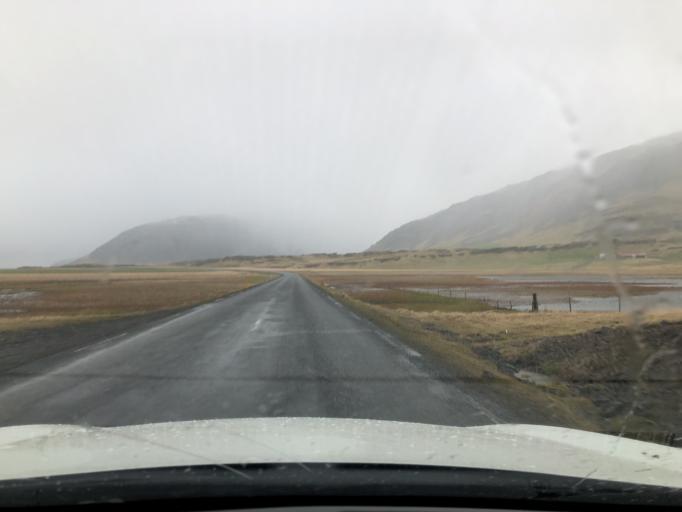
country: IS
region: East
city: Hoefn
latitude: 64.3695
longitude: -15.2737
